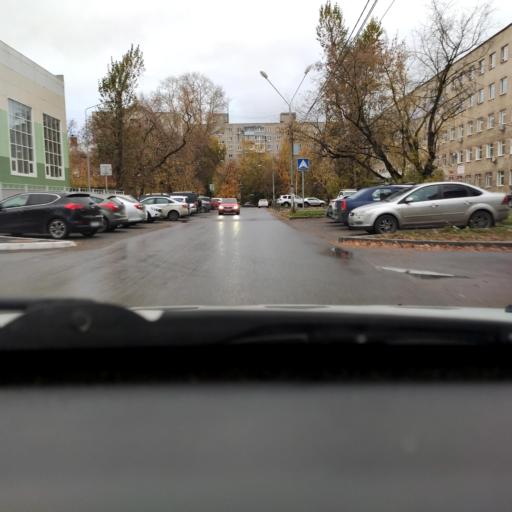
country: RU
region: Perm
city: Perm
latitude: 58.0115
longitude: 56.2135
